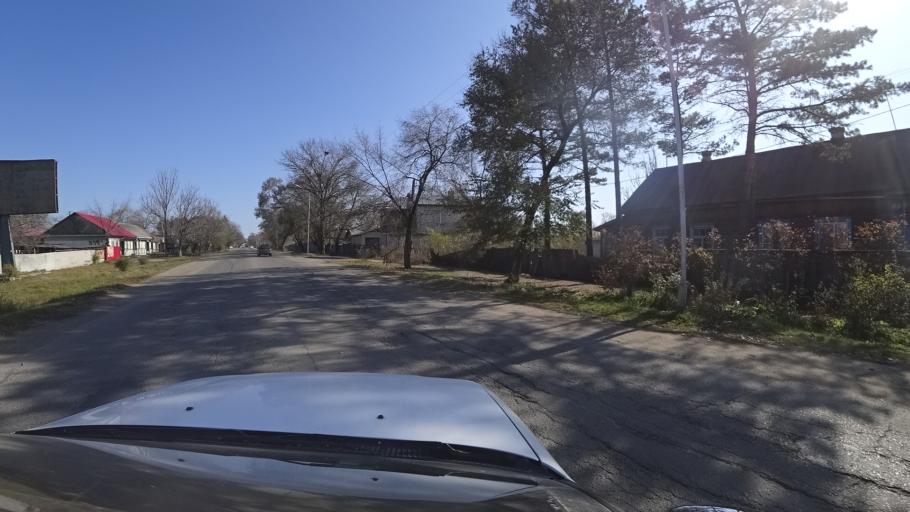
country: RU
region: Primorskiy
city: Dal'nerechensk
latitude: 45.9260
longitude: 133.7381
